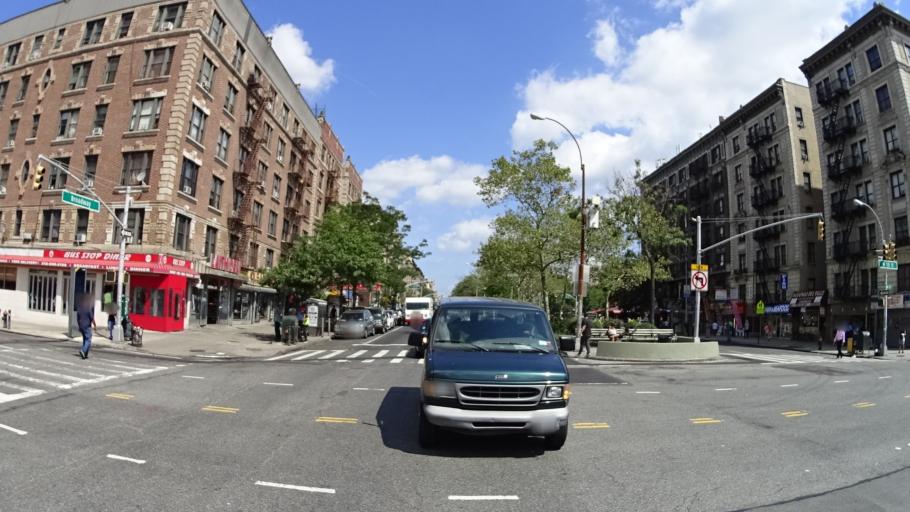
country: US
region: New Jersey
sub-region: Bergen County
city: Edgewater
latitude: 40.8201
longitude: -73.9552
